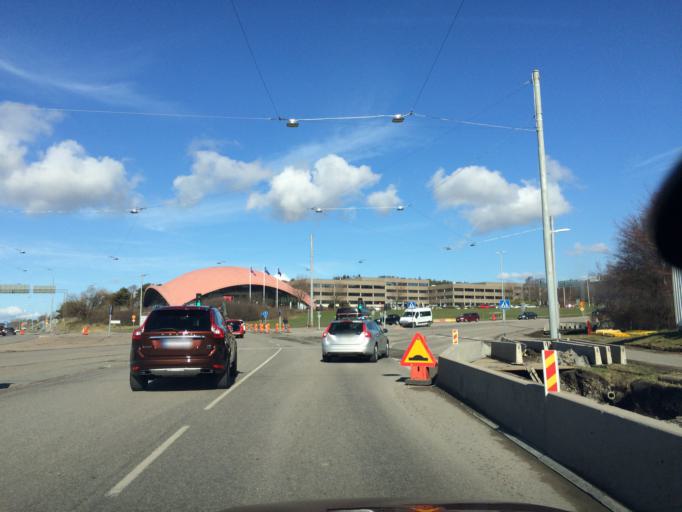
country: SE
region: Vaestra Goetaland
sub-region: Goteborg
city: Majorna
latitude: 57.7224
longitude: 11.8481
